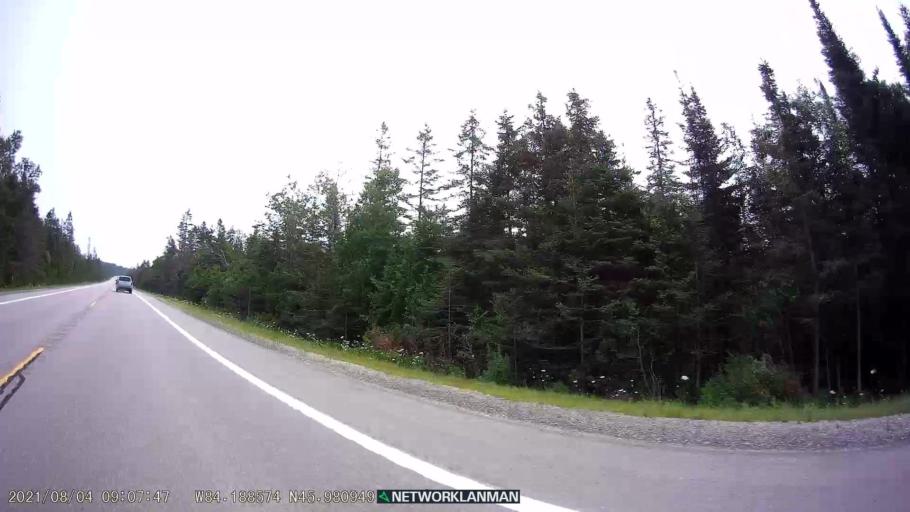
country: US
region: Michigan
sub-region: Cheboygan County
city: Cheboygan
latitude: 45.9810
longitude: -84.1881
